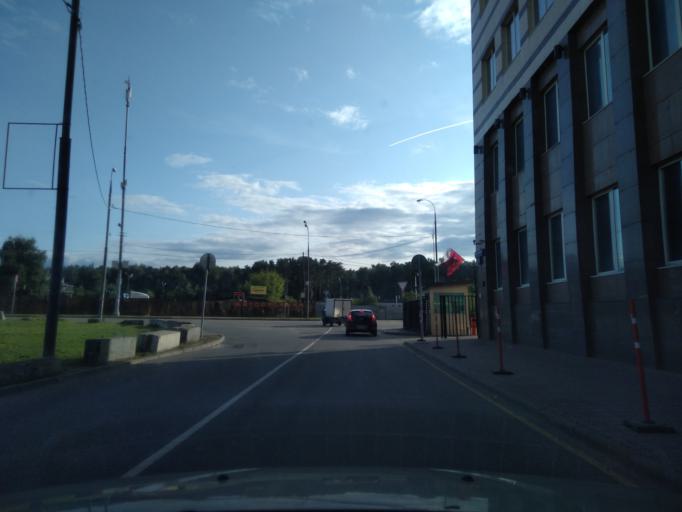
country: RU
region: Moscow
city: Rublevo
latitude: 55.7900
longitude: 37.3807
